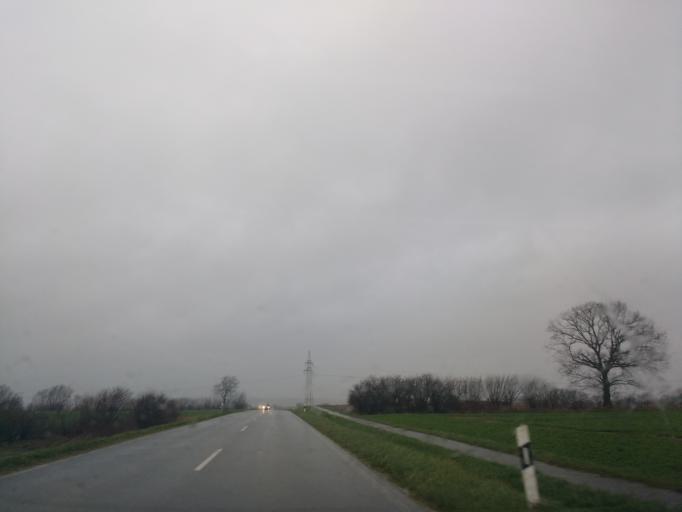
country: DE
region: Schleswig-Holstein
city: Blekendorf
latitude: 54.2891
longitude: 10.6784
